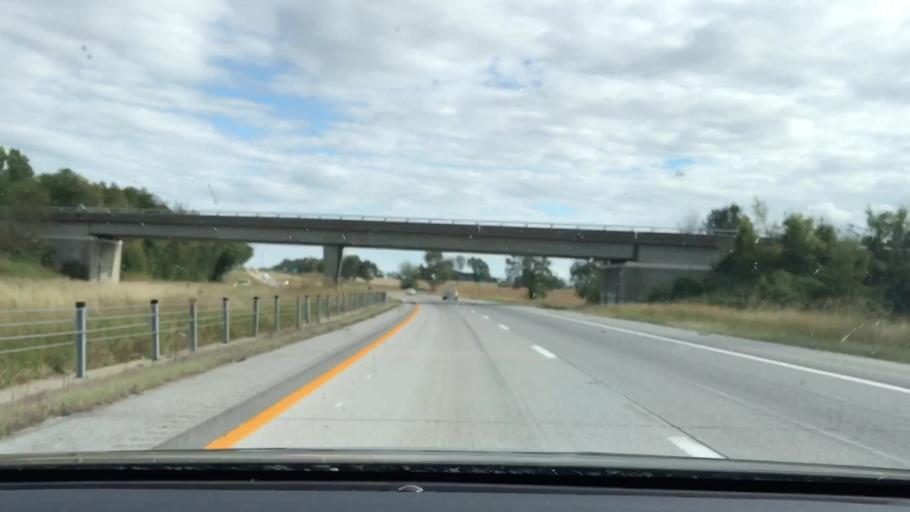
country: US
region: Kentucky
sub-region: Christian County
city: Hopkinsville
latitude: 36.8298
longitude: -87.6614
